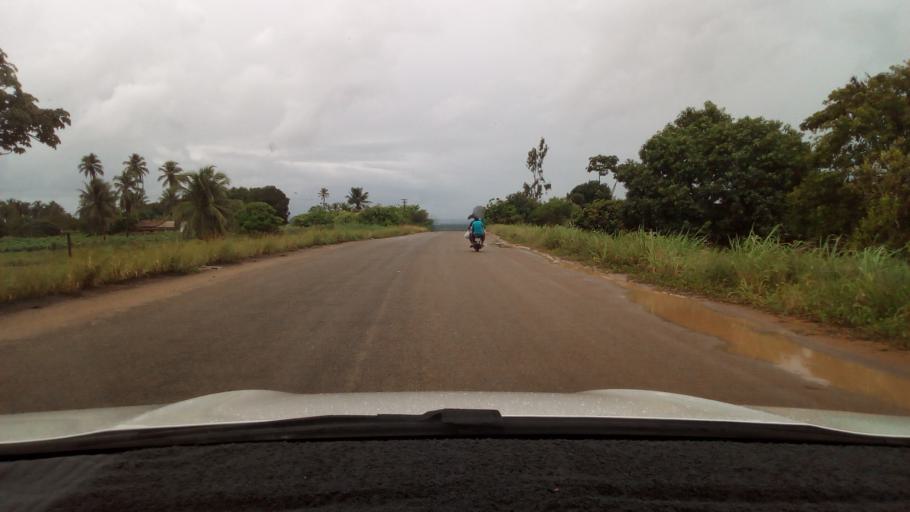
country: BR
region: Paraiba
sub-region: Pitimbu
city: Pitimbu
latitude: -7.4266
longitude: -34.8355
